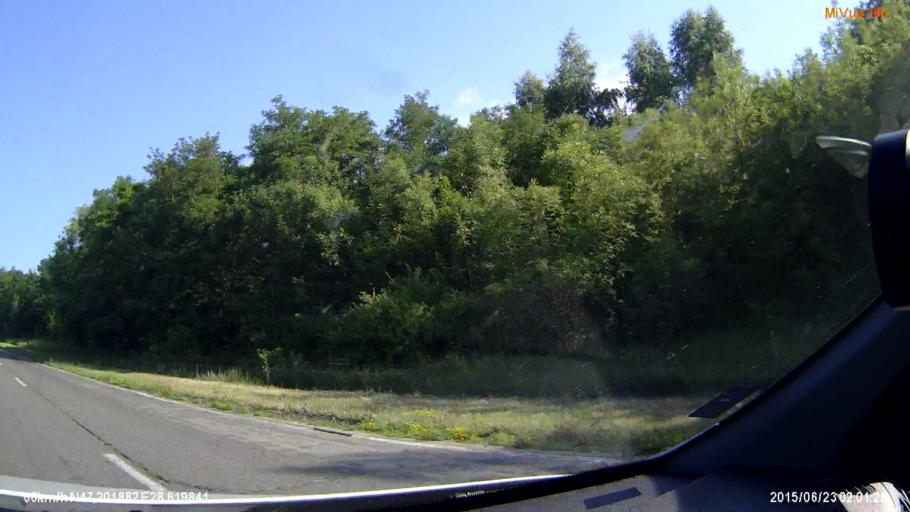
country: MD
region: Straseni
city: Straseni
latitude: 47.2022
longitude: 28.6195
